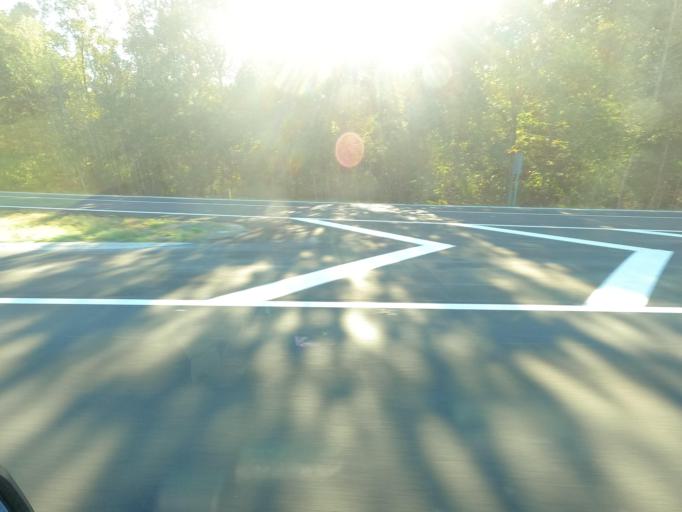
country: US
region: Tennessee
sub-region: Coffee County
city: Manchester
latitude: 35.4190
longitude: -86.0183
